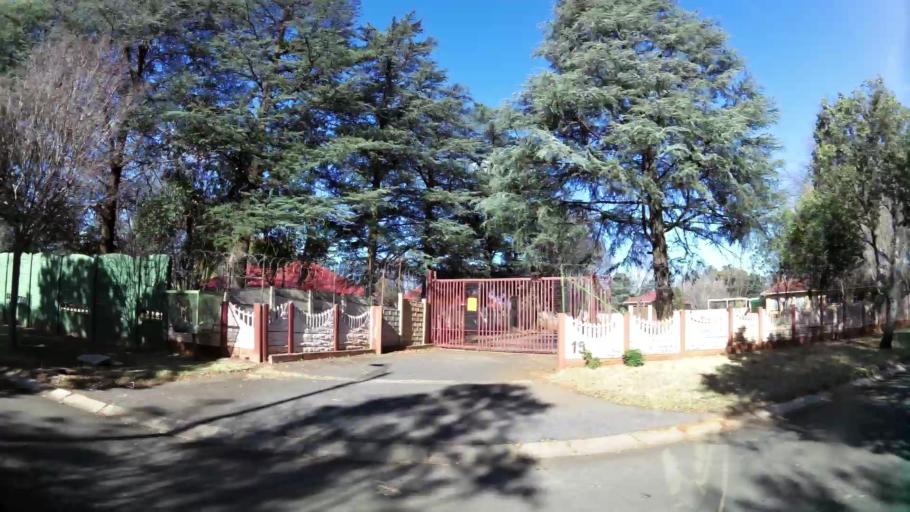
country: ZA
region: Gauteng
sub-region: West Rand District Municipality
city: Carletonville
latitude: -26.3700
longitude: 27.4079
